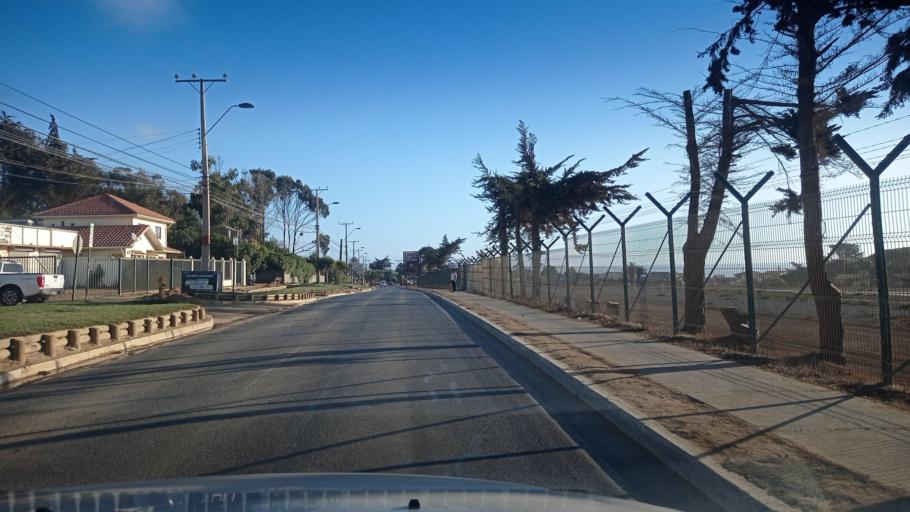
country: CL
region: O'Higgins
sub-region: Provincia de Colchagua
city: Santa Cruz
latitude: -34.3975
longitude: -72.0207
